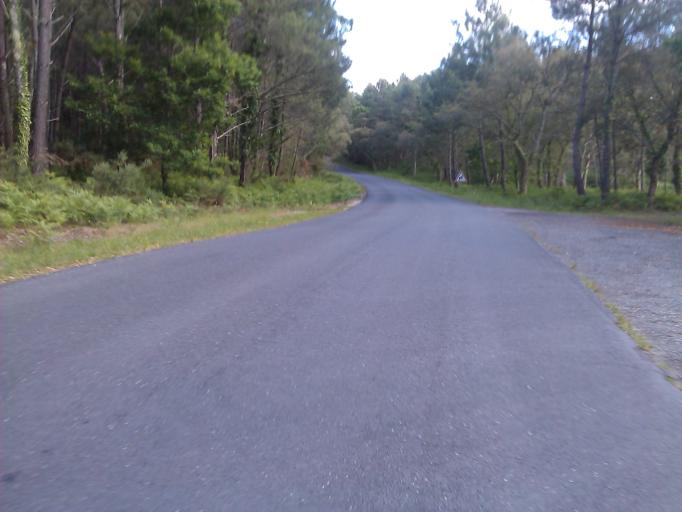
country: FR
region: Aquitaine
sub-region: Departement des Landes
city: Leon
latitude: 43.8705
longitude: -1.3618
